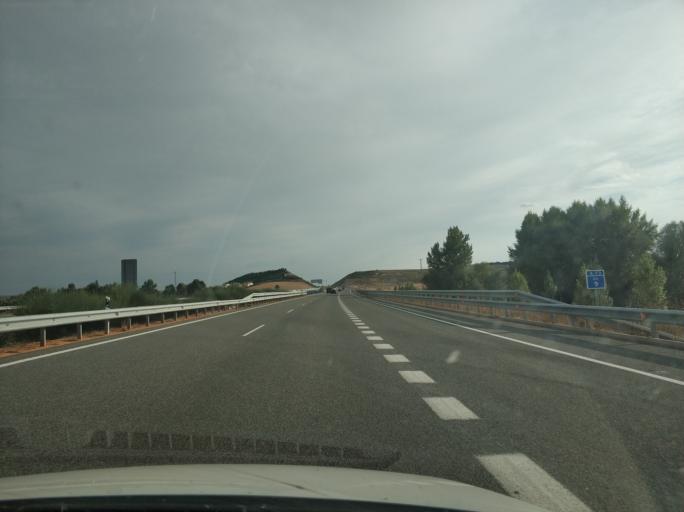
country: ES
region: Castille and Leon
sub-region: Provincia de Burgos
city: Quintanaortuno
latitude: 42.4598
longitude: -3.6885
